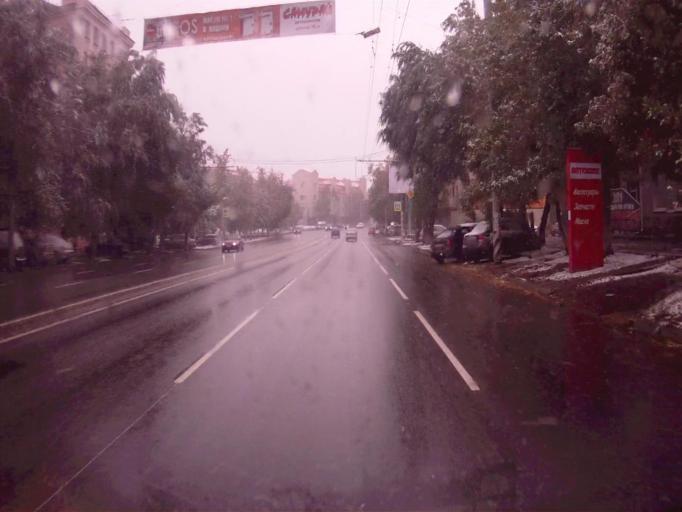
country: RU
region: Chelyabinsk
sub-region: Gorod Chelyabinsk
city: Chelyabinsk
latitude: 55.1486
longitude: 61.4161
